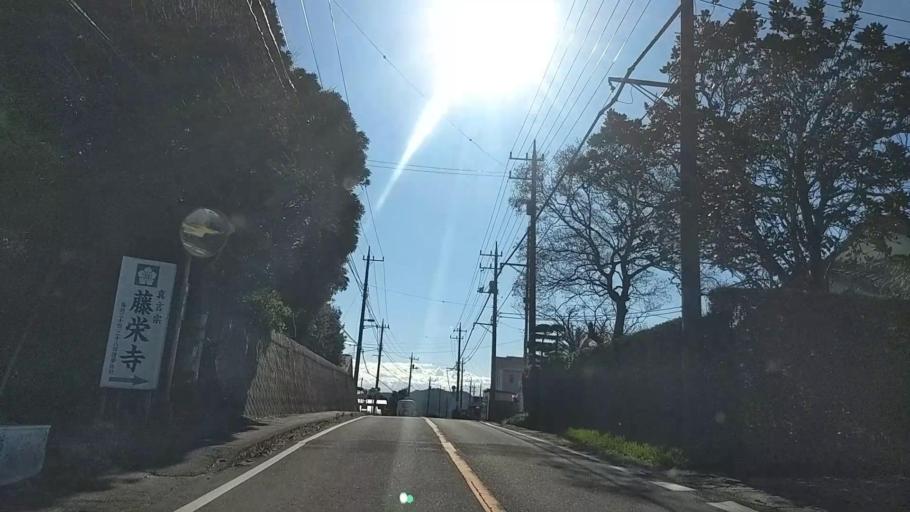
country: JP
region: Chiba
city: Tateyama
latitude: 34.9461
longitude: 139.8361
